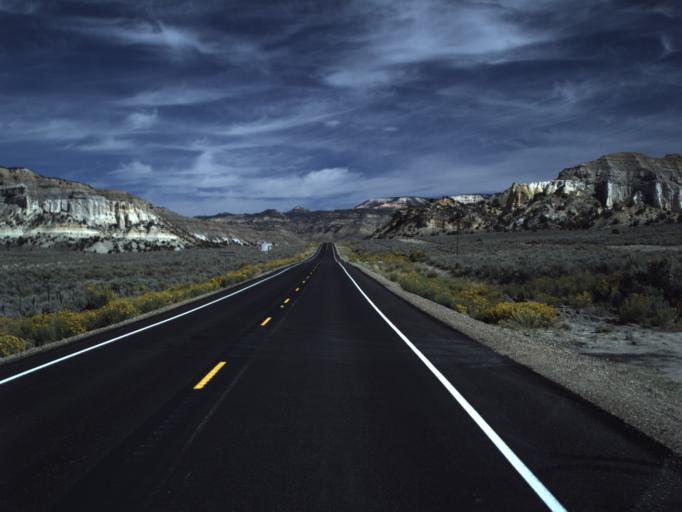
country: US
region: Utah
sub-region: Garfield County
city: Panguitch
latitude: 37.5713
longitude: -111.9887
